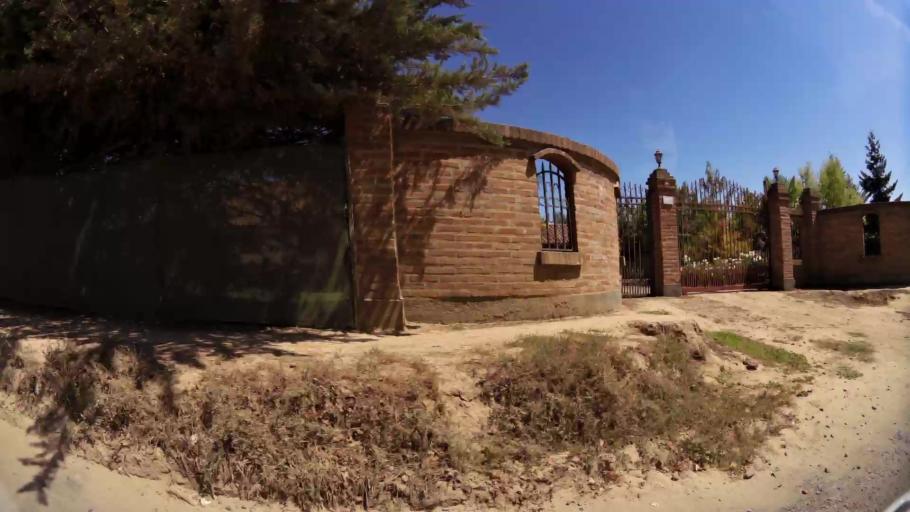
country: CL
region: Maule
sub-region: Provincia de Talca
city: Talca
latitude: -35.4254
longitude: -71.6126
